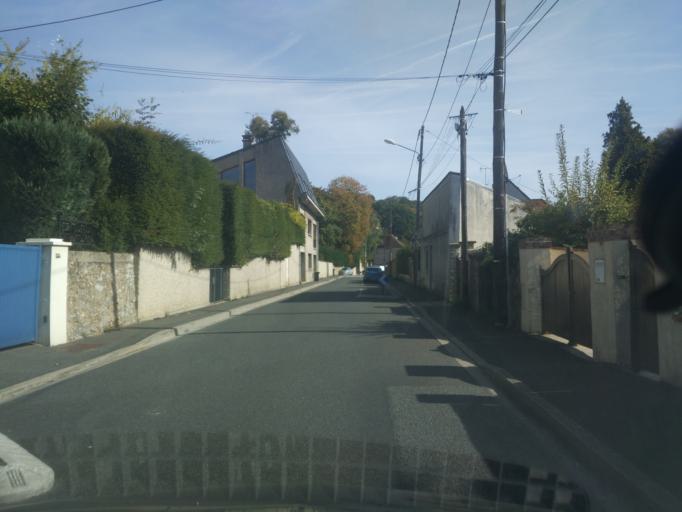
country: FR
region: Ile-de-France
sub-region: Departement de l'Essonne
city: Limours
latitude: 48.6478
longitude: 2.0732
